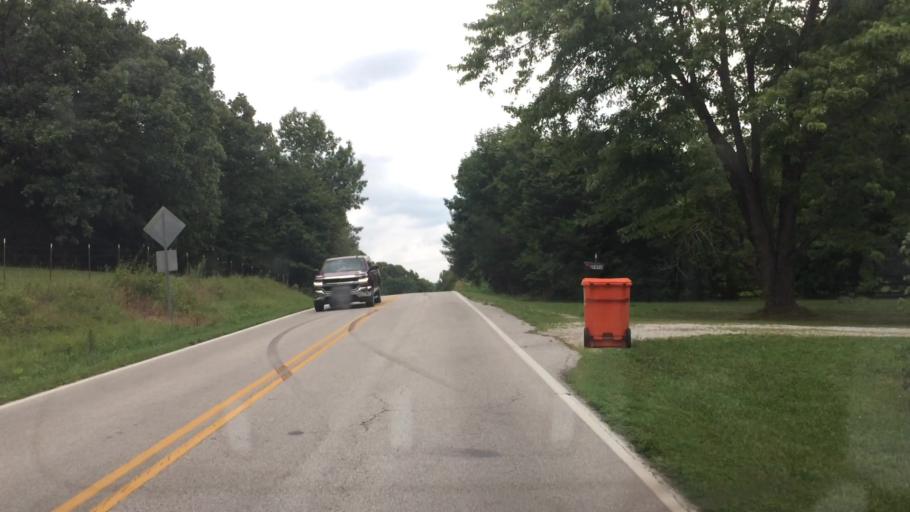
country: US
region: Missouri
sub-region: Greene County
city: Strafford
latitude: 37.2974
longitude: -93.0839
